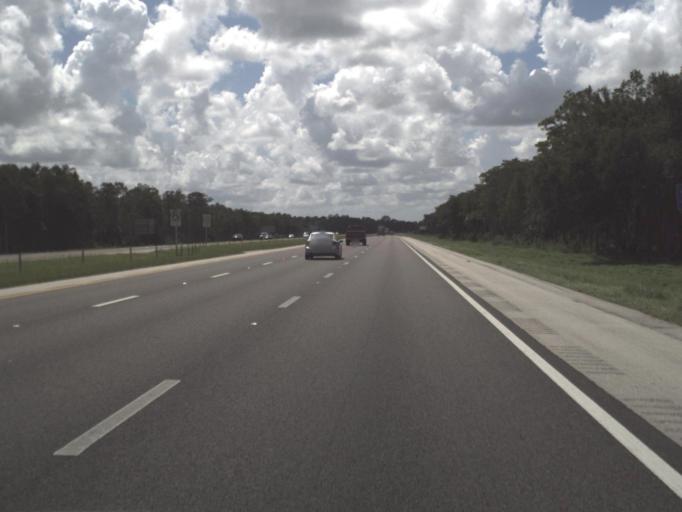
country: US
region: Florida
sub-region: Lee County
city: Bonita Springs
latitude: 26.3165
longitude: -81.7464
